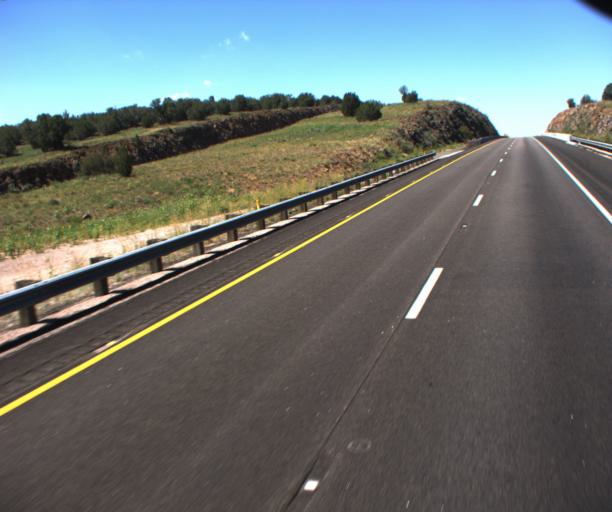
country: US
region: Arizona
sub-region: Mohave County
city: Peach Springs
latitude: 35.2428
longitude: -113.1966
